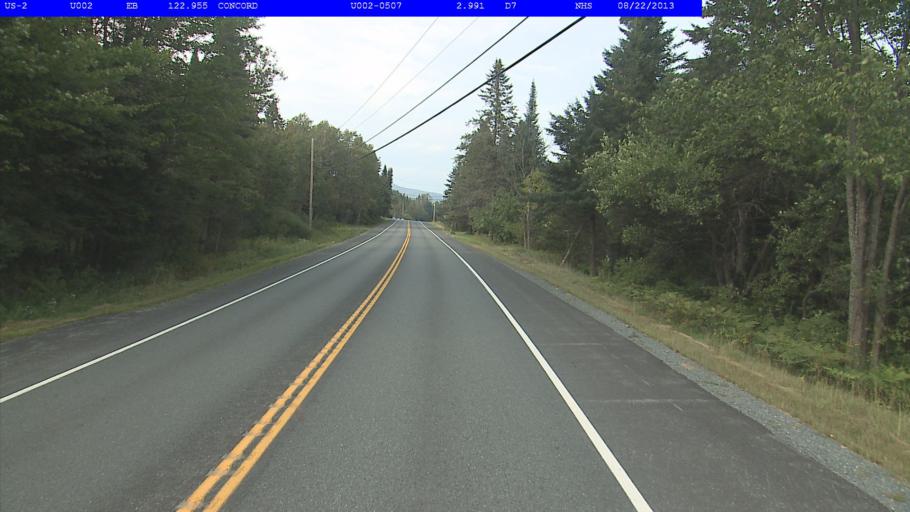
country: US
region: Vermont
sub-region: Caledonia County
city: St Johnsbury
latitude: 44.4375
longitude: -71.8787
